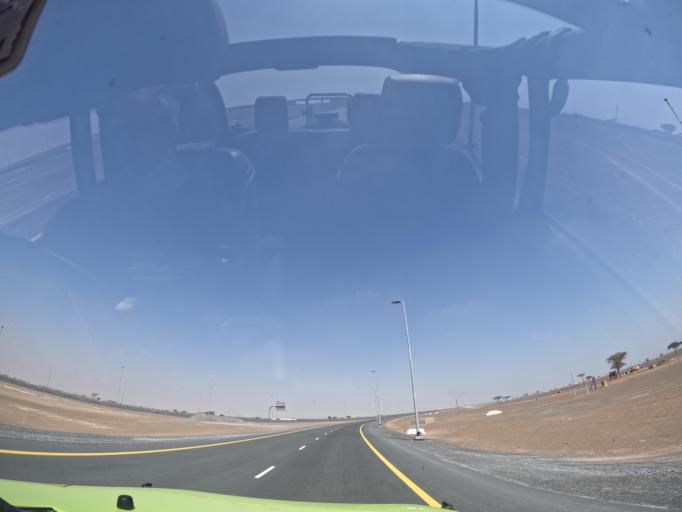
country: AE
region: Ash Shariqah
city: Adh Dhayd
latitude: 24.9139
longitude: 55.8031
